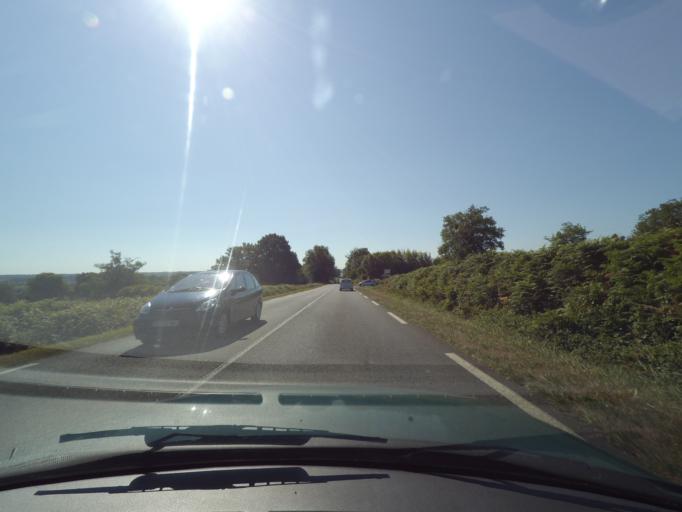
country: FR
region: Limousin
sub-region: Departement de la Haute-Vienne
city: Bussiere-Poitevine
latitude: 46.1819
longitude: 0.9374
